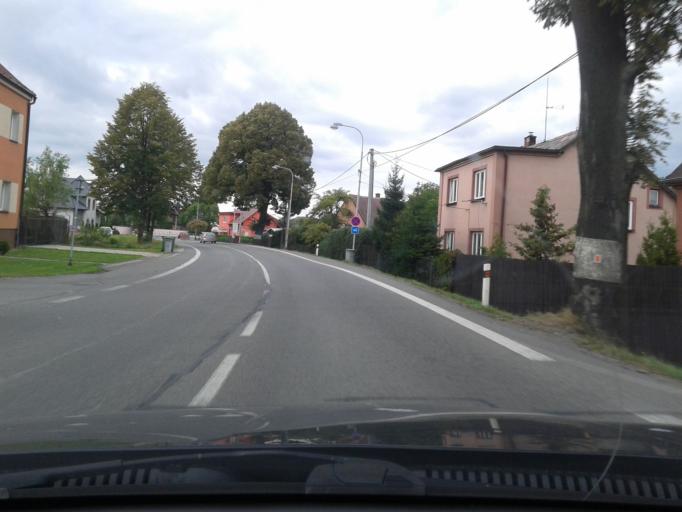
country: CZ
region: Moravskoslezsky
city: Orlova
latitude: 49.8603
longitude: 18.4459
